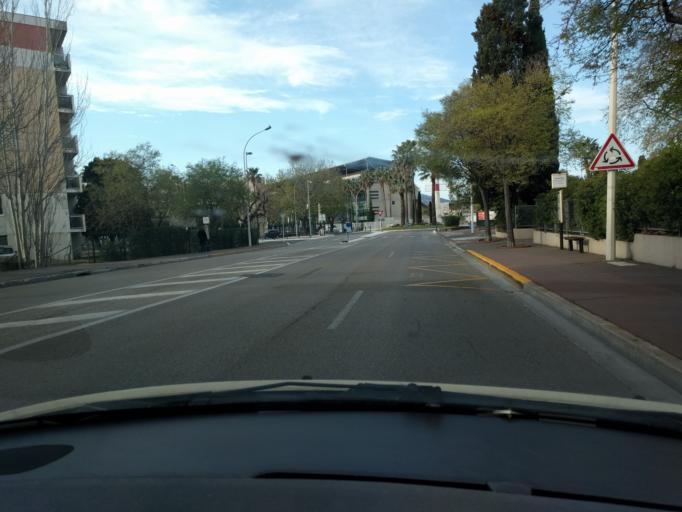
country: FR
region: Provence-Alpes-Cote d'Azur
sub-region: Departement des Alpes-Maritimes
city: Mandelieu-la-Napoule
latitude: 43.5549
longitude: 6.9667
